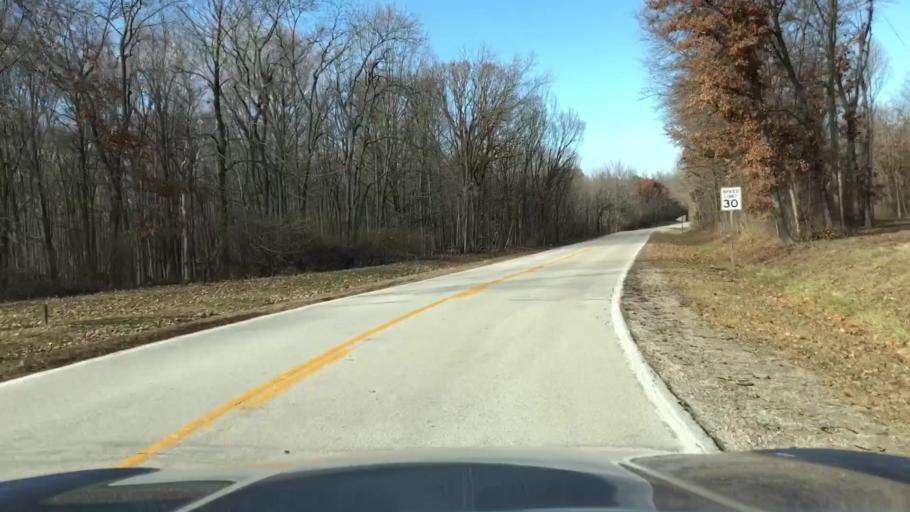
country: US
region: Illinois
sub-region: McLean County
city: Hudson
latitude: 40.6530
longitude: -88.9231
